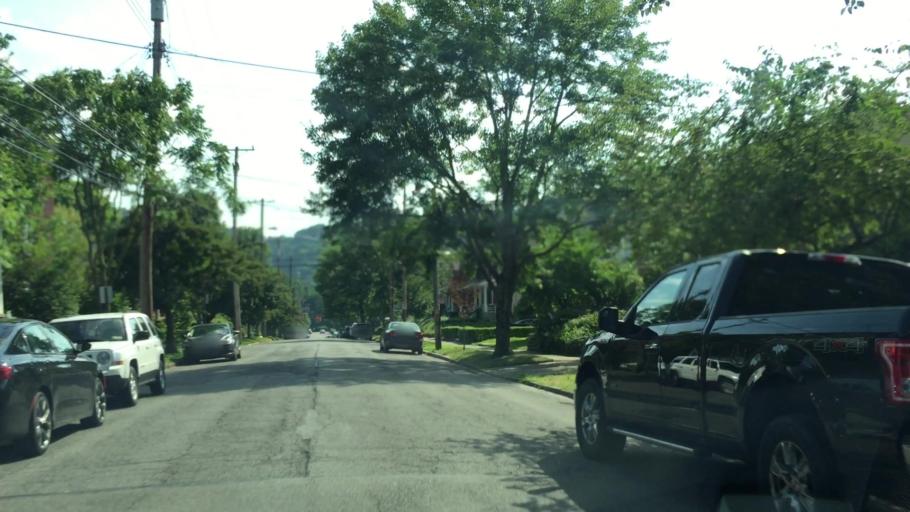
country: US
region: Pennsylvania
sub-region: Allegheny County
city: Sewickley
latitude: 40.5374
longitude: -80.1814
